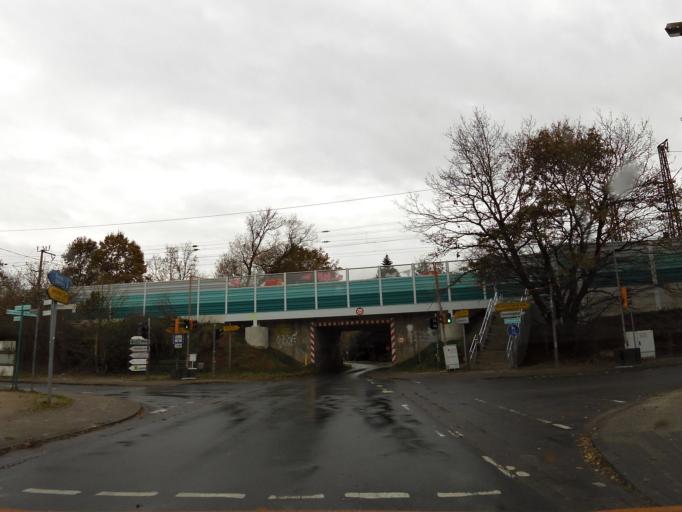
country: DE
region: Lower Saxony
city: Hude
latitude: 53.1117
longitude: 8.4523
